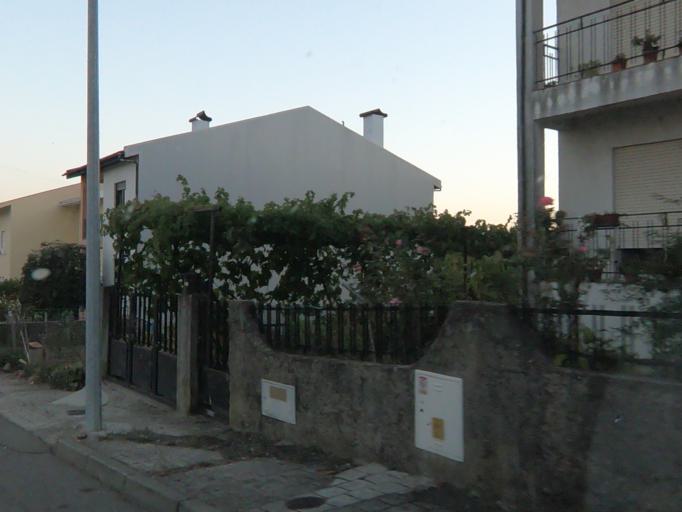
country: PT
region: Vila Real
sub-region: Vila Real
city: Vila Real
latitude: 41.3089
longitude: -7.7683
